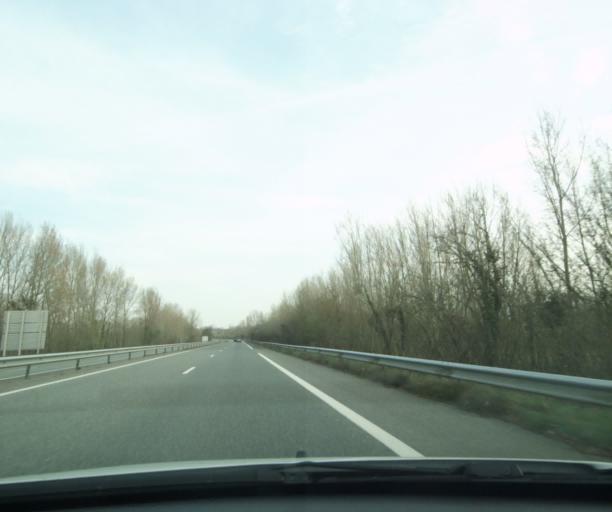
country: FR
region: Midi-Pyrenees
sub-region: Departement des Hautes-Pyrenees
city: Juillan
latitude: 43.2132
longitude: 0.0333
